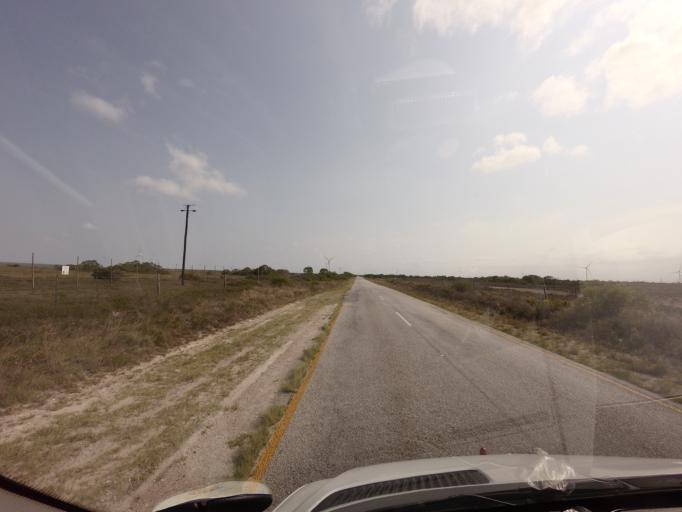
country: ZA
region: Eastern Cape
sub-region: Nelson Mandela Bay Metropolitan Municipality
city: Uitenhage
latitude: -33.6840
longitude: 25.5888
